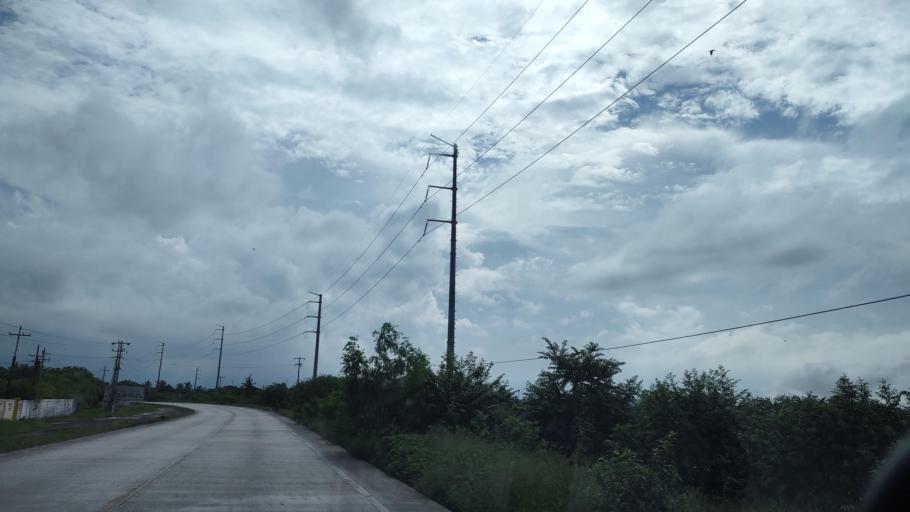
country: MX
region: Veracruz
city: Anahuac
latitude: 22.2069
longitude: -97.8700
